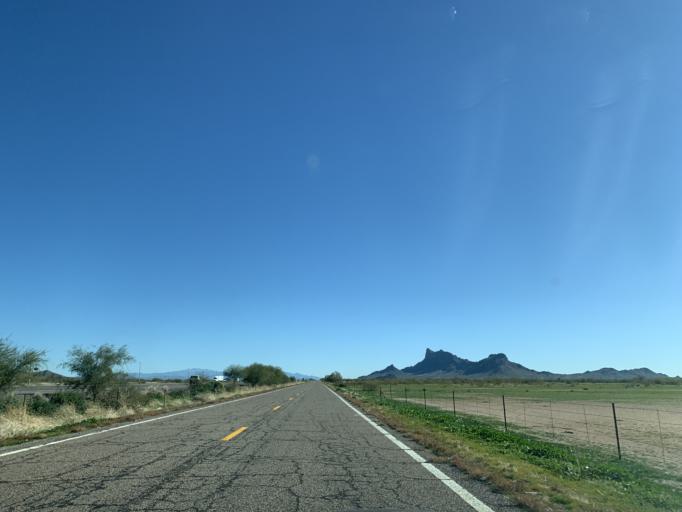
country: US
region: Arizona
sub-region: Pinal County
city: Eloy
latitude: 32.6898
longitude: -111.4583
